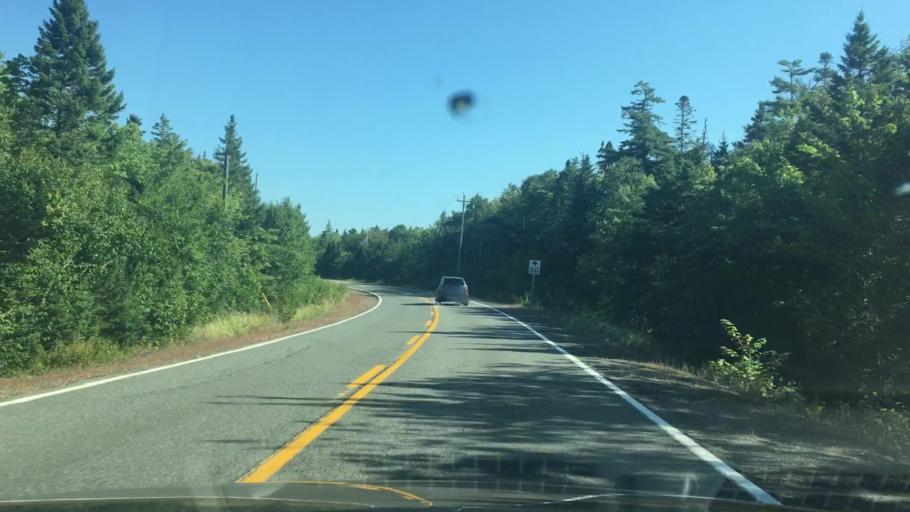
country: CA
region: Nova Scotia
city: Cole Harbour
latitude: 44.8002
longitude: -62.8819
